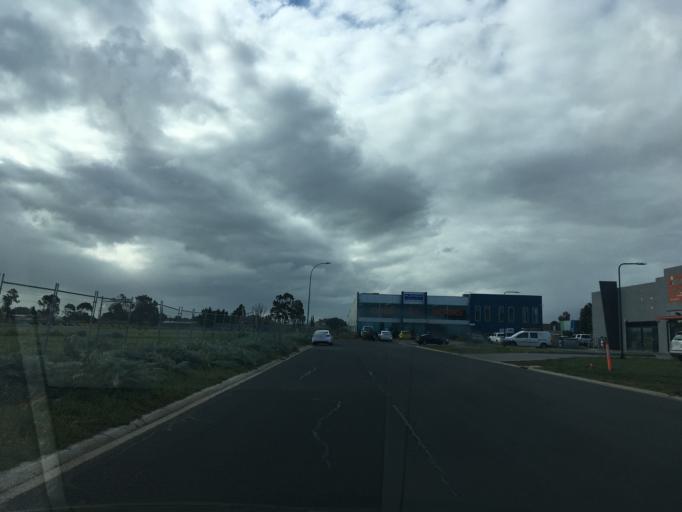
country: AU
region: Victoria
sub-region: Wyndham
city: Hoppers Crossing
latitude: -37.8735
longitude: 144.7171
